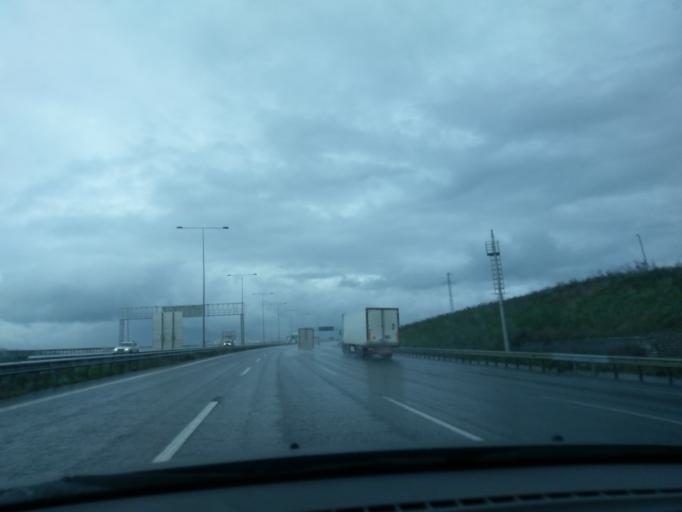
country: TR
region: Istanbul
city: Basaksehir
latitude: 41.1278
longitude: 28.8070
